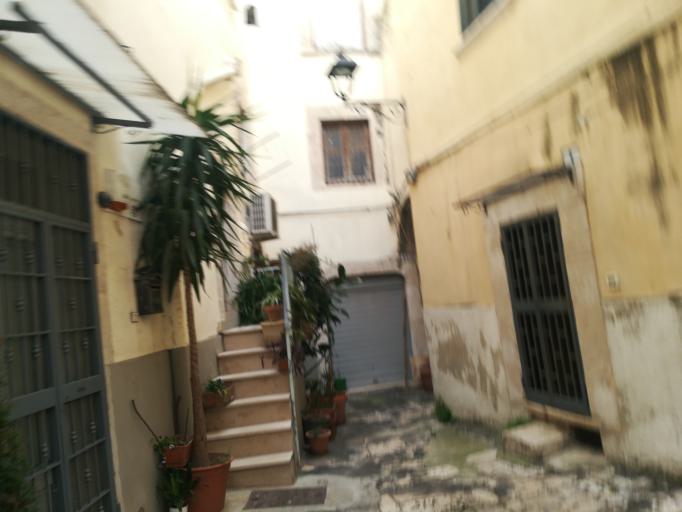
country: IT
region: Apulia
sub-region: Provincia di Bari
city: Bitonto
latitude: 41.1051
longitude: 16.6916
